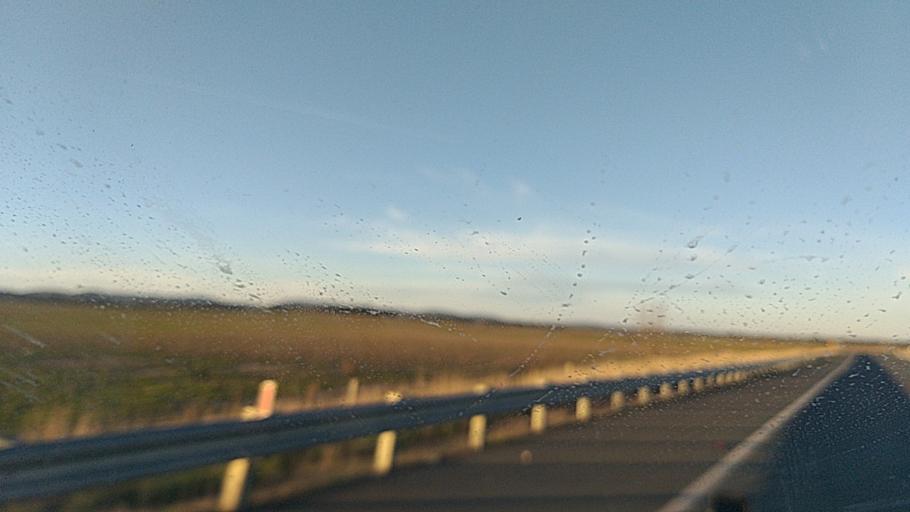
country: AU
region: New South Wales
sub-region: Goulburn Mulwaree
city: Goulburn
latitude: -34.8502
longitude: 149.5555
